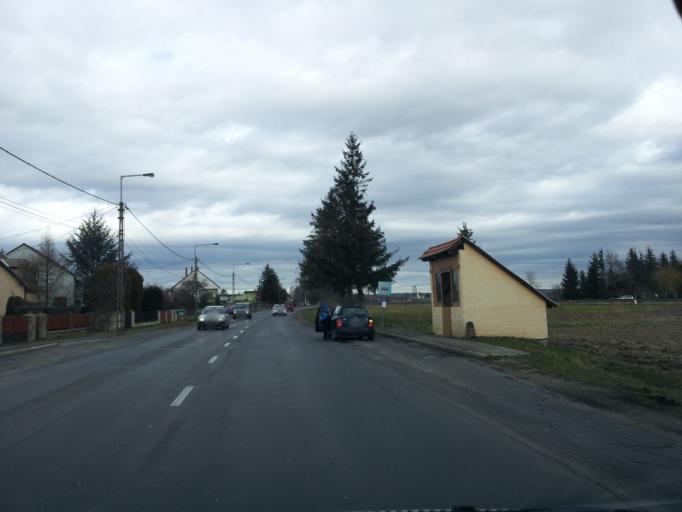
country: HU
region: Vas
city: Gencsapati
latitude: 47.3192
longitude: 16.5868
